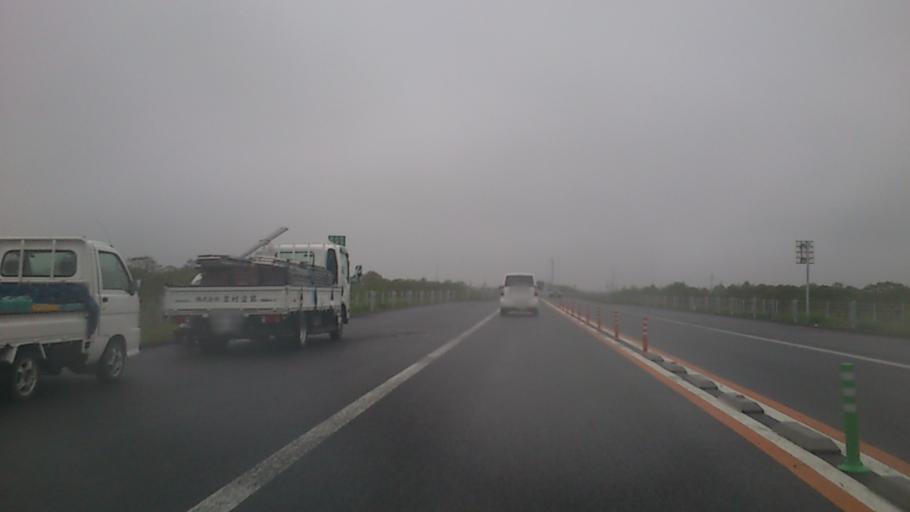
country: JP
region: Hokkaido
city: Kushiro
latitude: 43.0323
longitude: 144.3934
